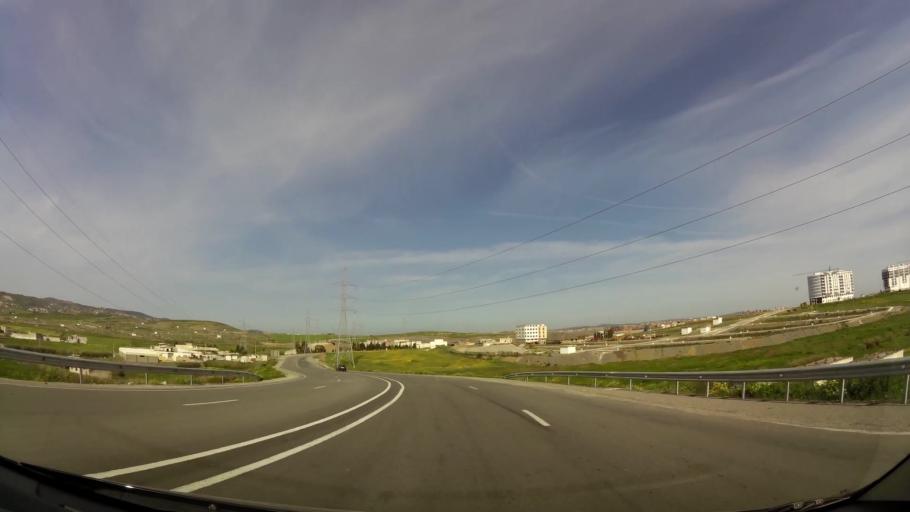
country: MA
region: Tanger-Tetouan
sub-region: Tanger-Assilah
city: Tangier
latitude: 35.7015
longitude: -5.8016
